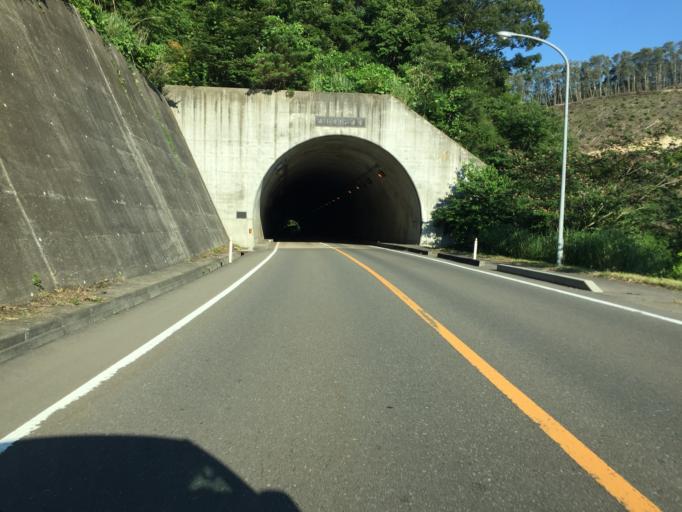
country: JP
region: Miyagi
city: Shiroishi
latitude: 37.9542
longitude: 140.5326
